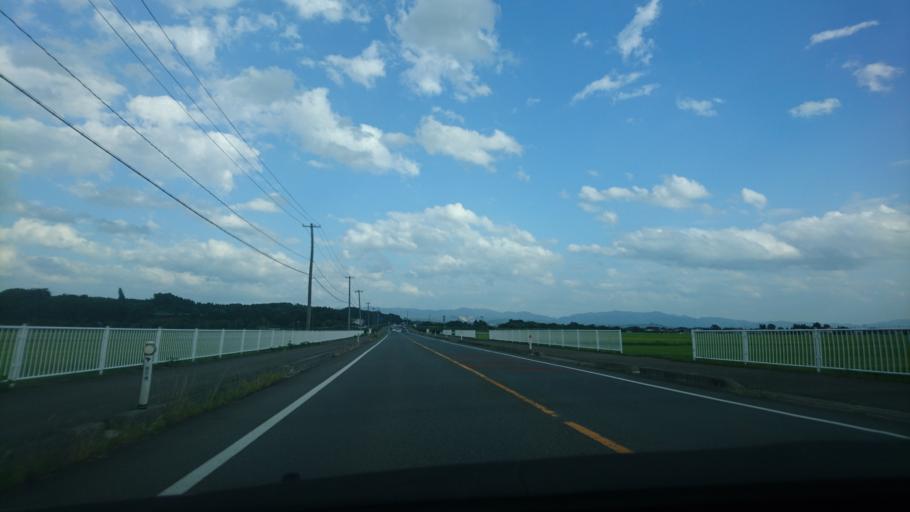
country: JP
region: Iwate
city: Mizusawa
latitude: 39.2086
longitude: 141.1541
